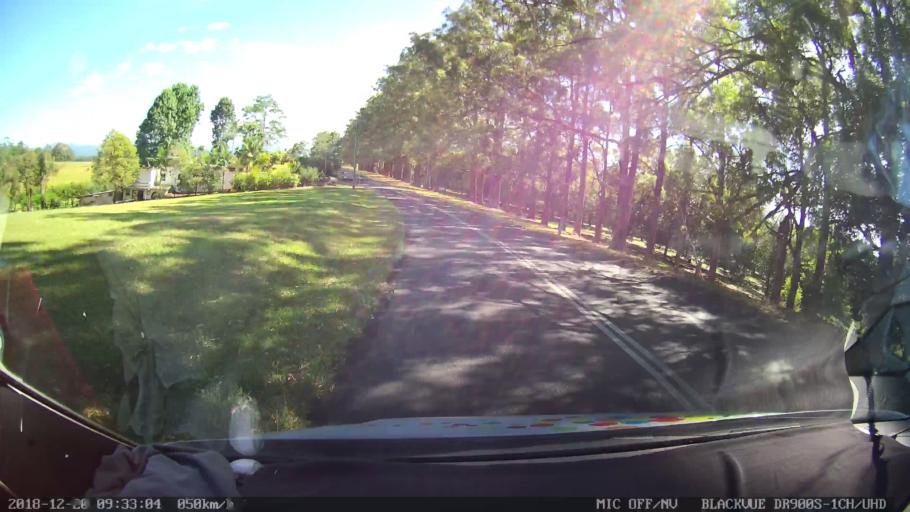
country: AU
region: New South Wales
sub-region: Lismore Municipality
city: Goonellabah
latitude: -28.6979
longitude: 153.3067
